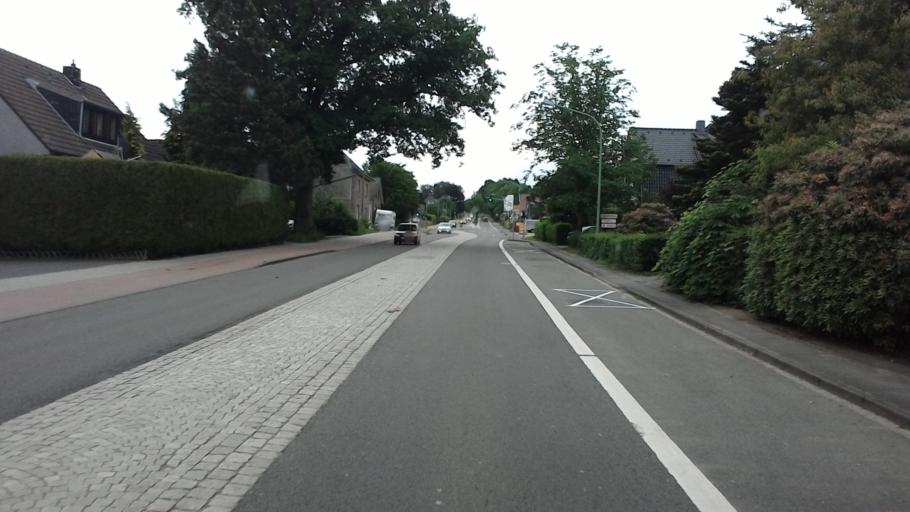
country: DE
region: North Rhine-Westphalia
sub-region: Regierungsbezirk Koln
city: Roetgen
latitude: 50.6422
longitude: 6.1900
